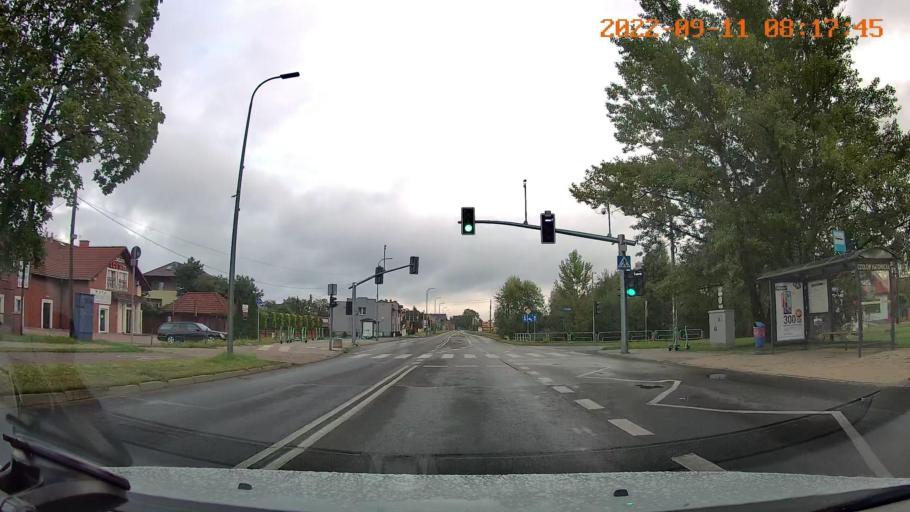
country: PL
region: Silesian Voivodeship
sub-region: Tychy
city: Tychy
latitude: 50.1406
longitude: 18.9956
